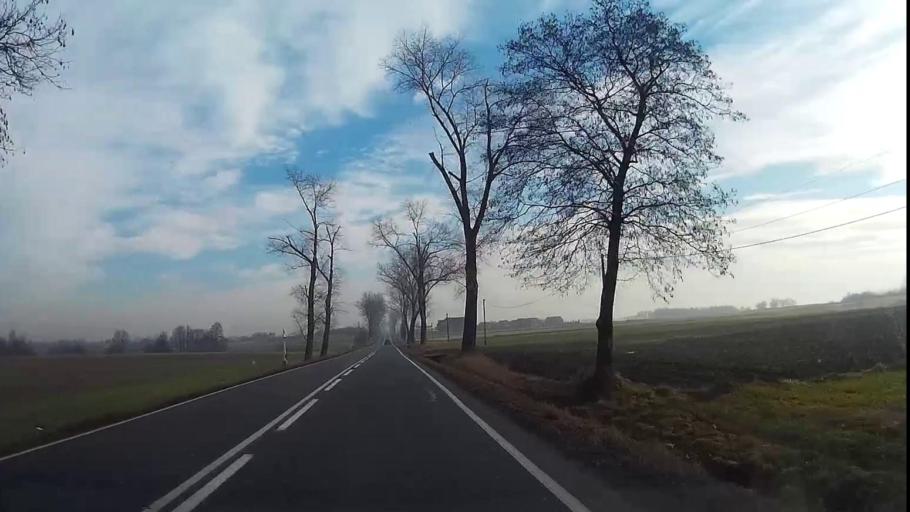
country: PL
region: Lesser Poland Voivodeship
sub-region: Powiat krakowski
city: Czulow
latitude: 50.0368
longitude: 19.6695
